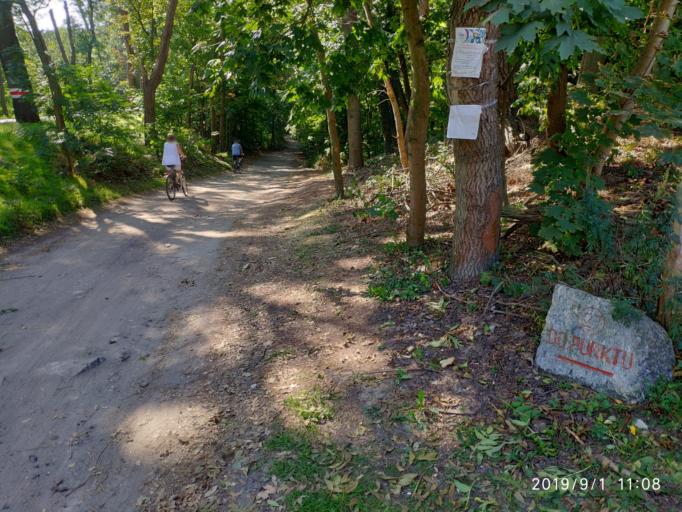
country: PL
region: Lubusz
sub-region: Powiat zielonogorski
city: Kargowa
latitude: 52.1084
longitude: 15.8365
